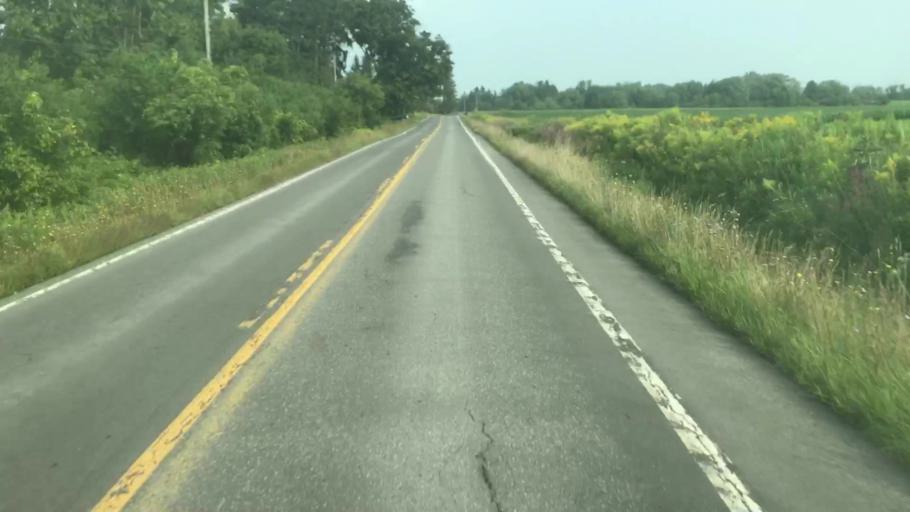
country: US
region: New York
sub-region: Onondaga County
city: Skaneateles
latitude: 42.8959
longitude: -76.4522
